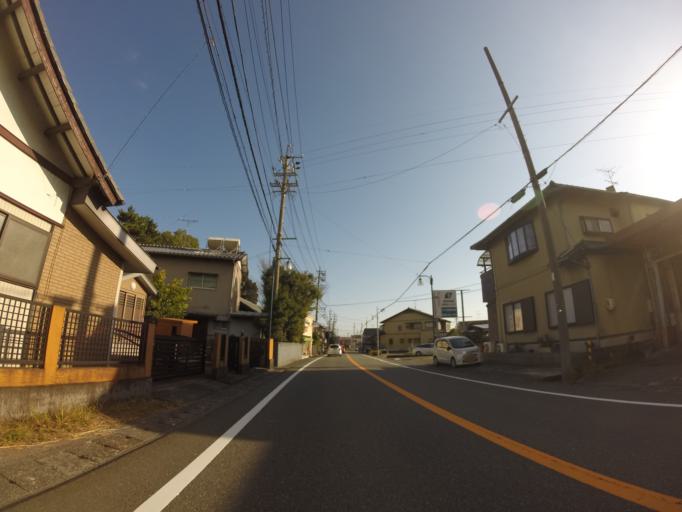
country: JP
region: Shizuoka
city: Shimada
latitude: 34.8095
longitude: 138.2187
